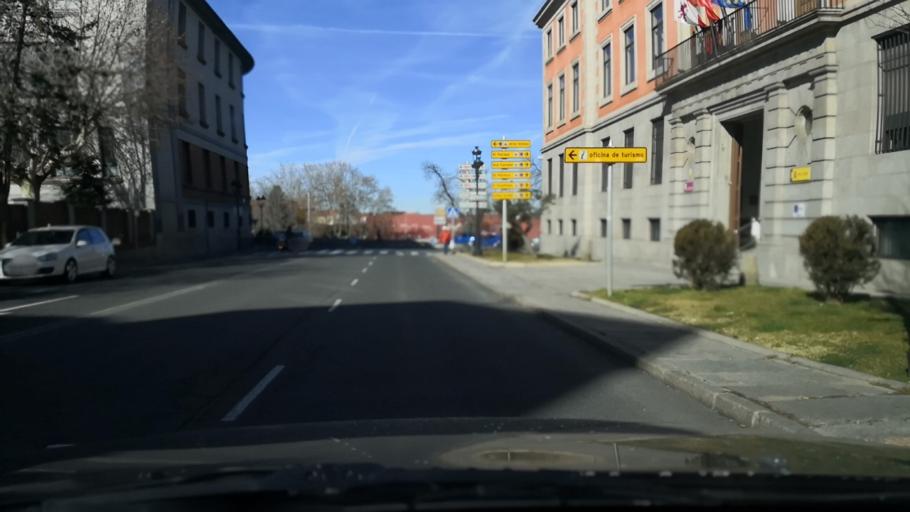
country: ES
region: Castille and Leon
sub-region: Provincia de Avila
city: Avila
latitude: 40.6565
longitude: -4.6879
